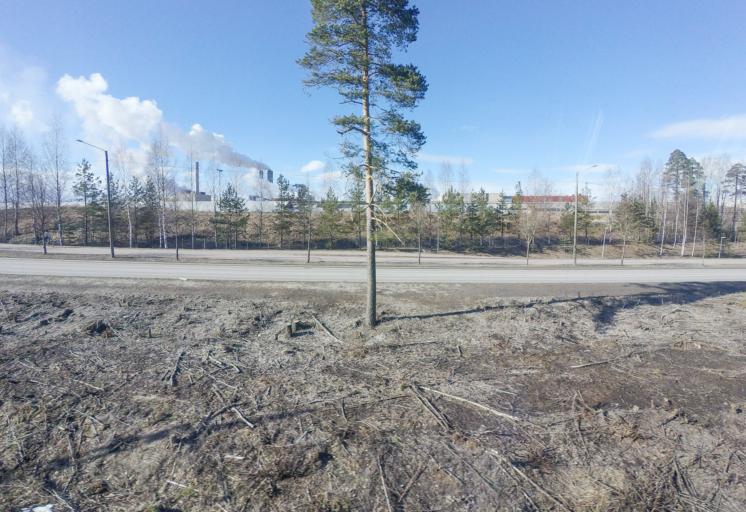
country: FI
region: South Karelia
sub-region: Lappeenranta
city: Lappeenranta
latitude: 61.0613
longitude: 28.2509
